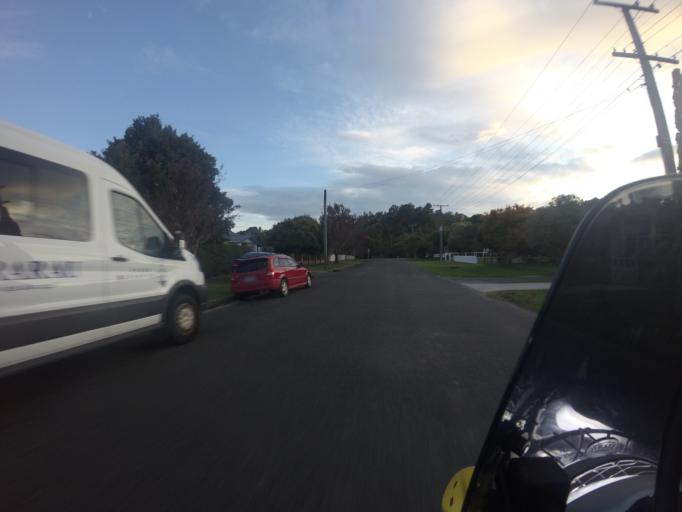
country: NZ
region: Gisborne
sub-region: Gisborne District
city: Gisborne
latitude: -38.6631
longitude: 178.0363
